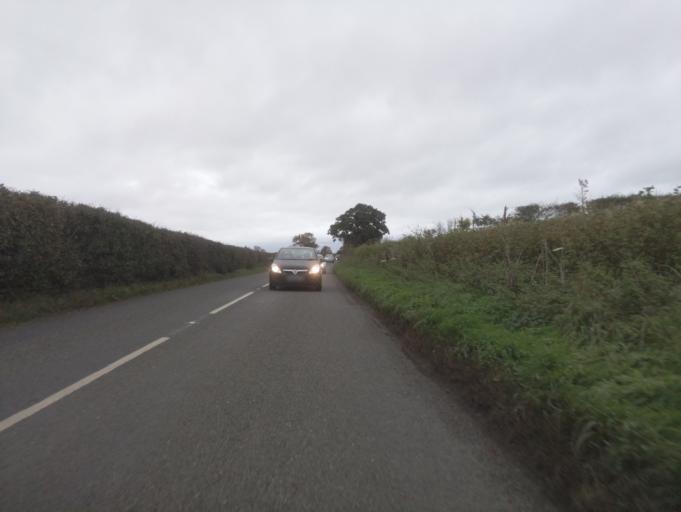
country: GB
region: England
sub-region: Dorset
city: Sherborne
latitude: 50.9759
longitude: -2.5600
